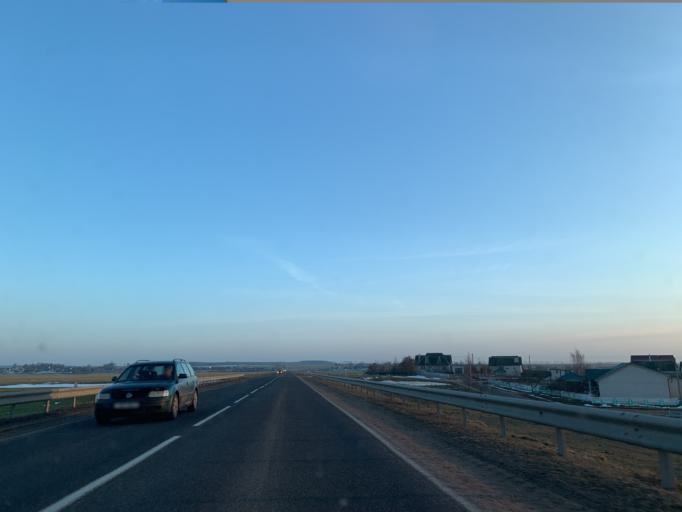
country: BY
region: Minsk
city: Haradzyeya
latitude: 53.3123
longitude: 26.5656
